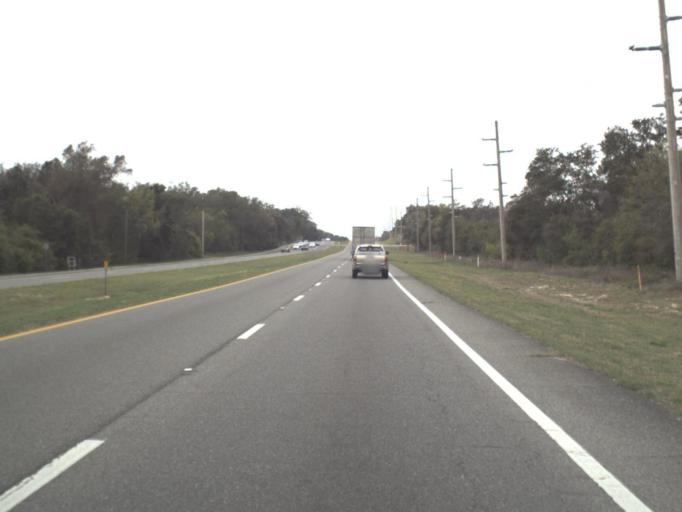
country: US
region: Florida
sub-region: Santa Rosa County
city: Gulf Breeze
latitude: 30.3643
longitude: -87.1353
